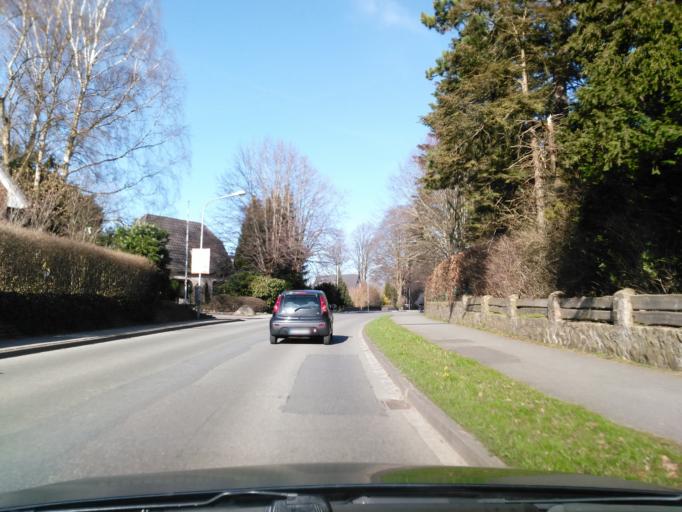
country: DE
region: Schleswig-Holstein
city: Felde
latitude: 54.3060
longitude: 9.9398
